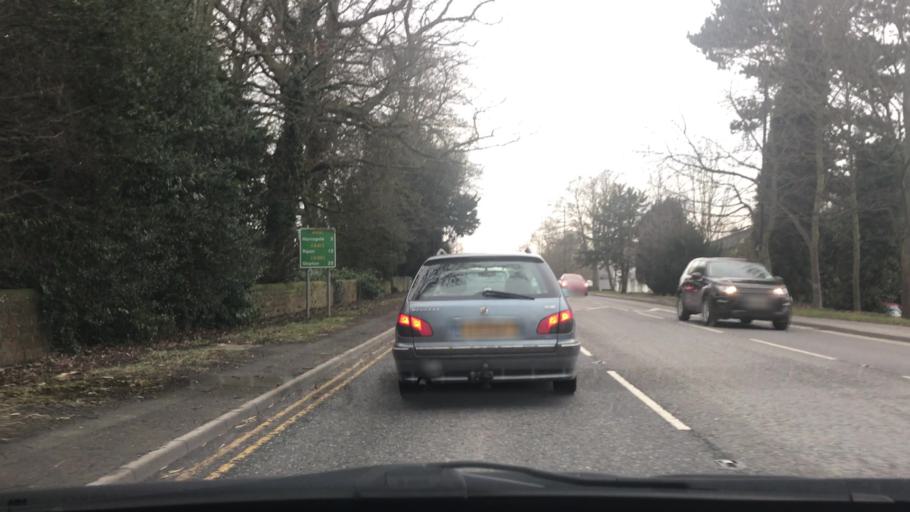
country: GB
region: England
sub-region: North Yorkshire
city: Knaresborough
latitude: 53.9839
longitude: -1.4907
